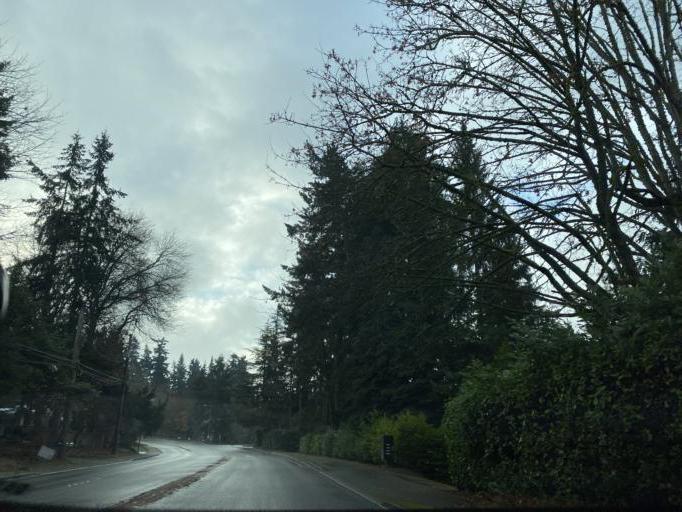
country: US
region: Washington
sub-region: King County
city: Mercer Island
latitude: 47.5686
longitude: -122.2270
